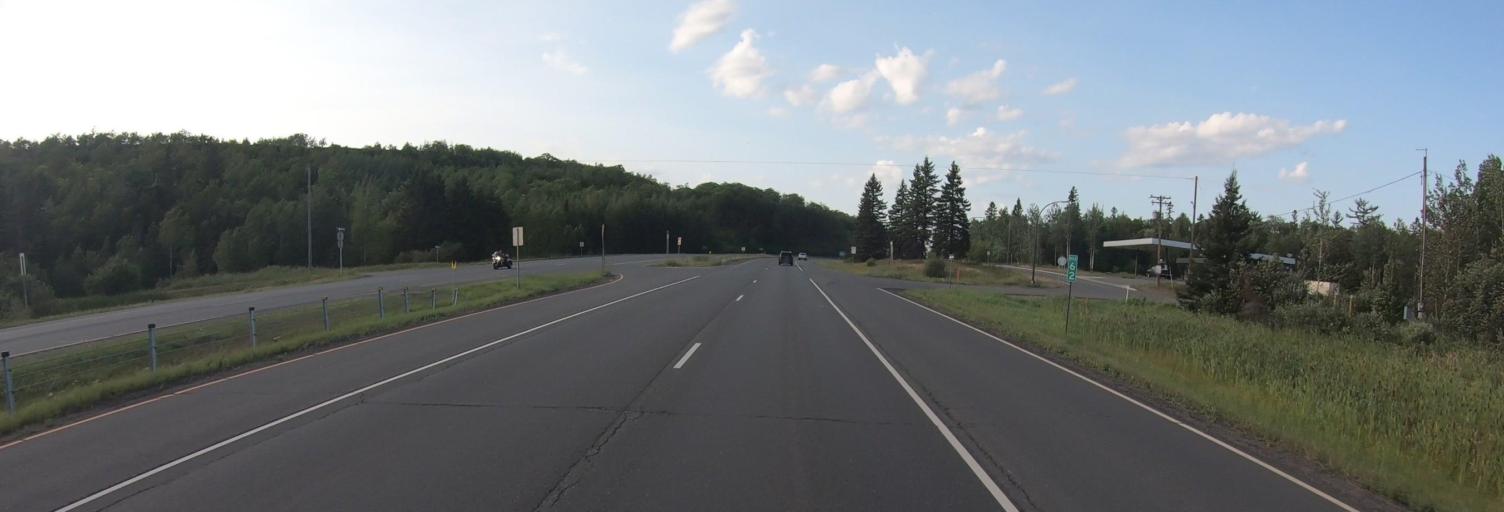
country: US
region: Minnesota
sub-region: Saint Louis County
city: Eveleth
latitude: 47.4835
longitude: -92.5307
